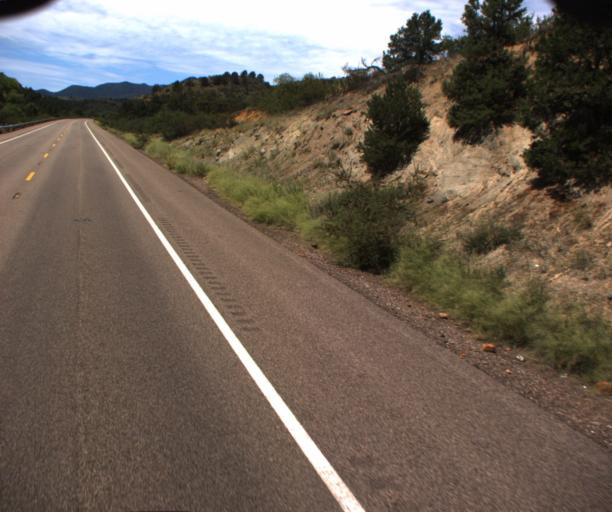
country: US
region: Arizona
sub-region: Gila County
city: Globe
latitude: 33.5692
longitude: -110.6653
